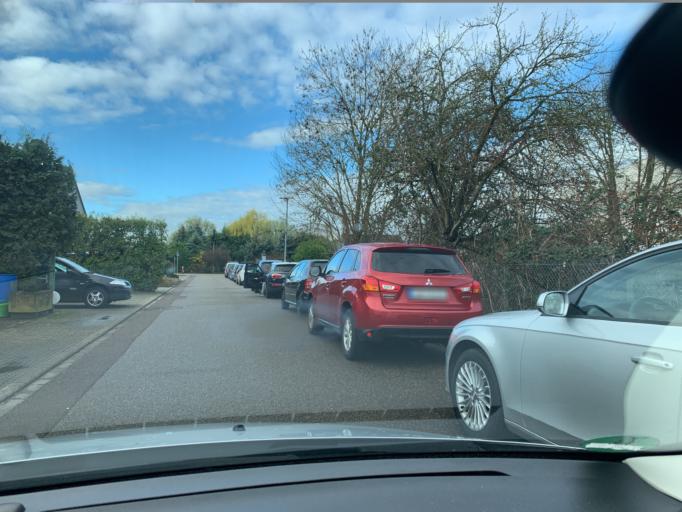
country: DE
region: Baden-Wuerttemberg
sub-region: Freiburg Region
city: Umkirch
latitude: 48.0437
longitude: 7.7661
